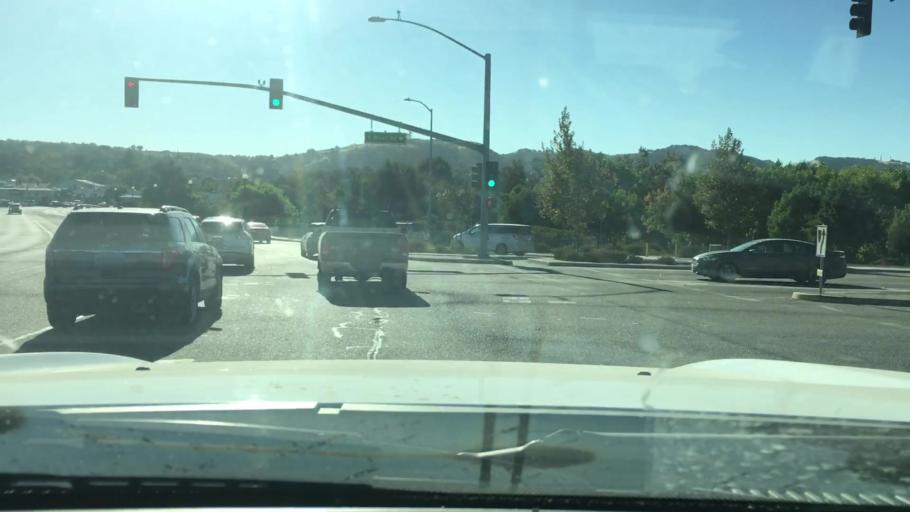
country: US
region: California
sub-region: San Luis Obispo County
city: Paso Robles
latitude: 35.6292
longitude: -120.6830
